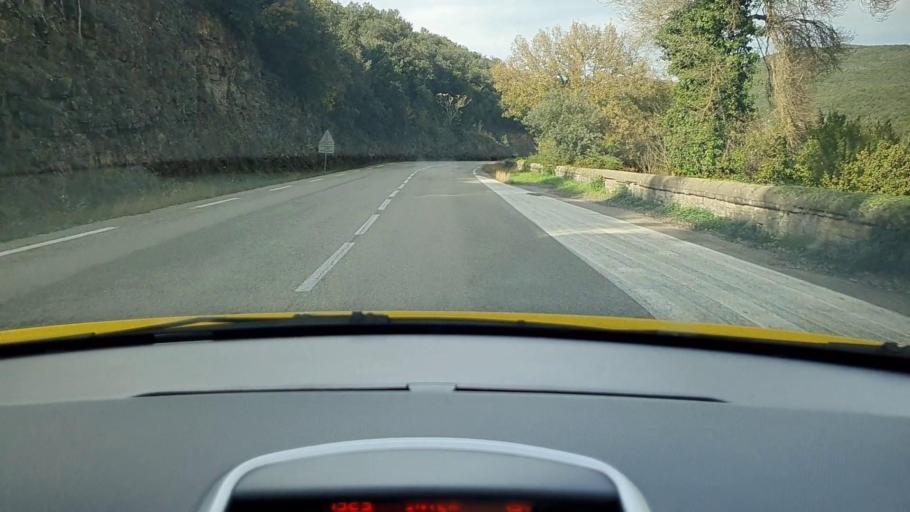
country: FR
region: Languedoc-Roussillon
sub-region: Departement du Gard
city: Anduze
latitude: 44.0683
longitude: 3.9354
